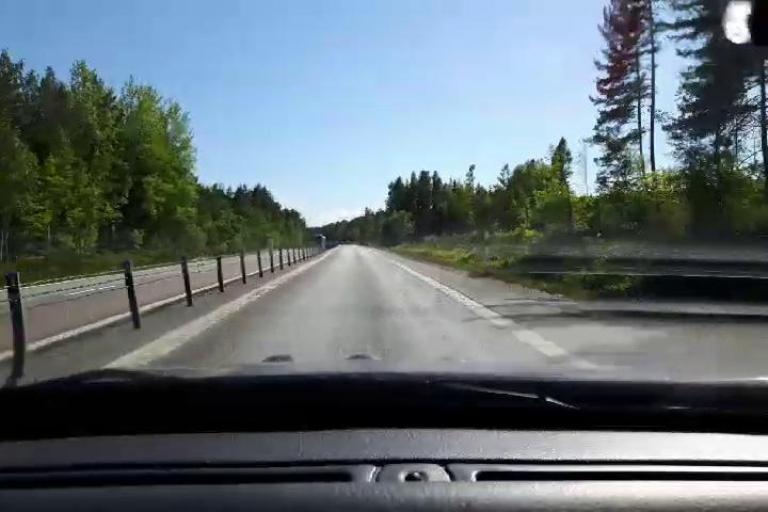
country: SE
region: Gaevleborg
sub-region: Gavle Kommun
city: Norrsundet
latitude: 60.9401
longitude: 17.0183
